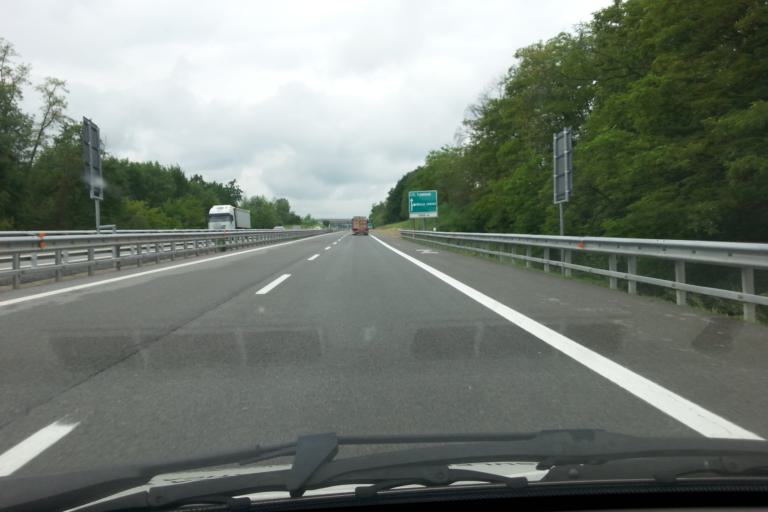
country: IT
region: Piedmont
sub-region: Provincia di Cuneo
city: Borgo
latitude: 44.4094
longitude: 7.9501
